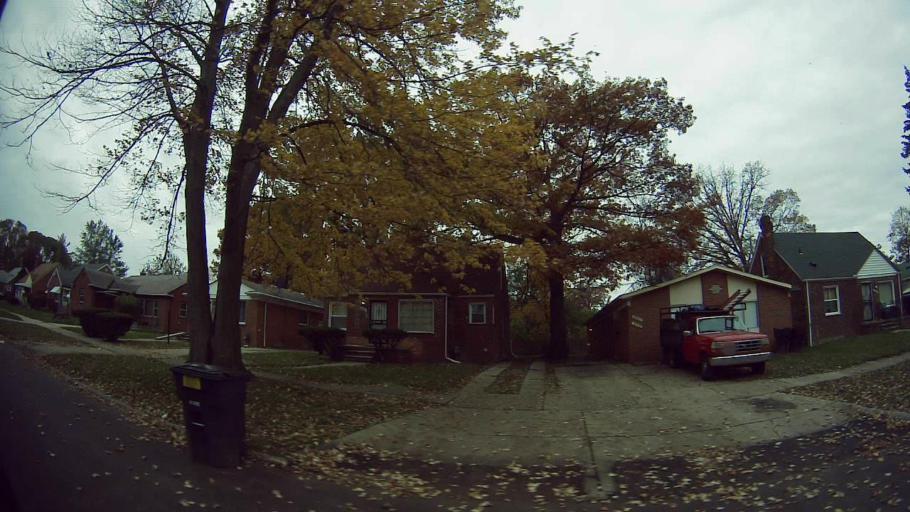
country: US
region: Michigan
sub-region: Oakland County
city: Oak Park
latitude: 42.4398
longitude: -83.1905
